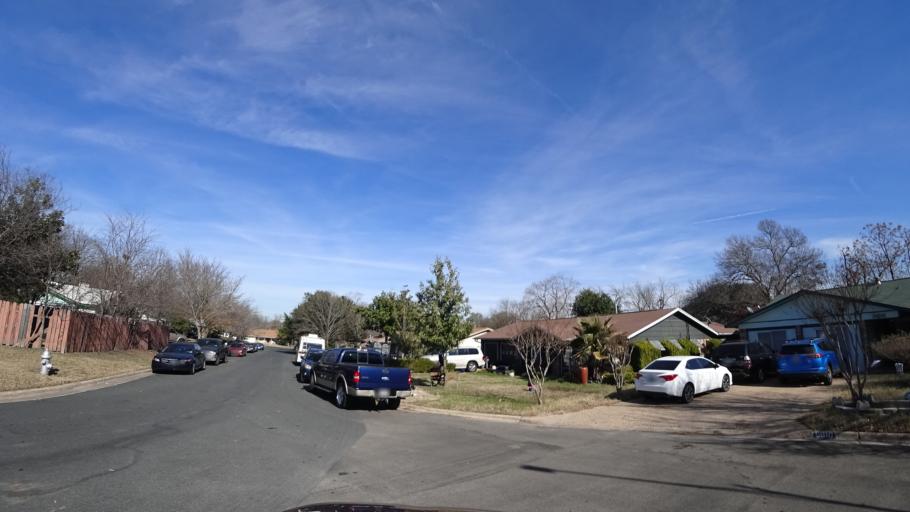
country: US
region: Texas
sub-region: Travis County
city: Wells Branch
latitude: 30.3711
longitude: -97.7075
